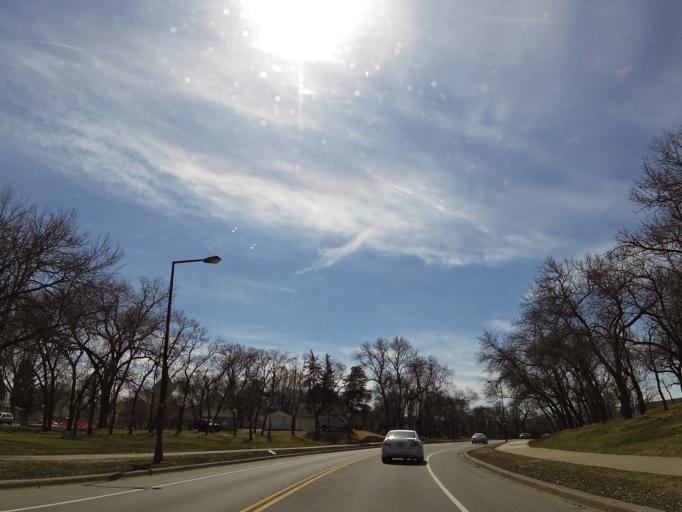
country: US
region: Minnesota
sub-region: Ramsey County
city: Maplewood
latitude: 44.9724
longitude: -93.0439
